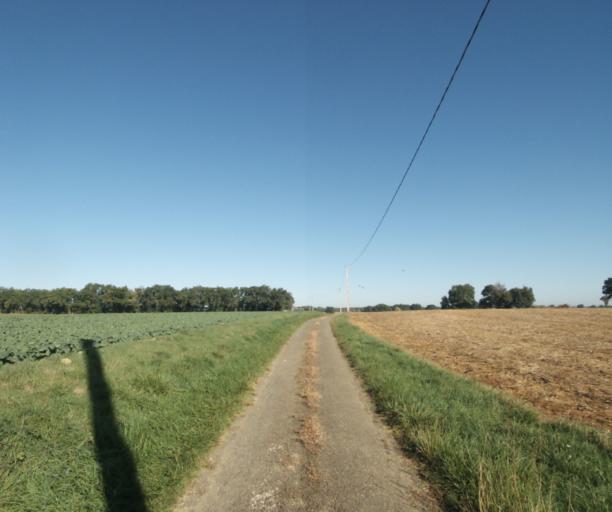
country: FR
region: Midi-Pyrenees
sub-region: Departement du Gers
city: Vic-Fezensac
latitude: 43.8186
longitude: 0.2696
